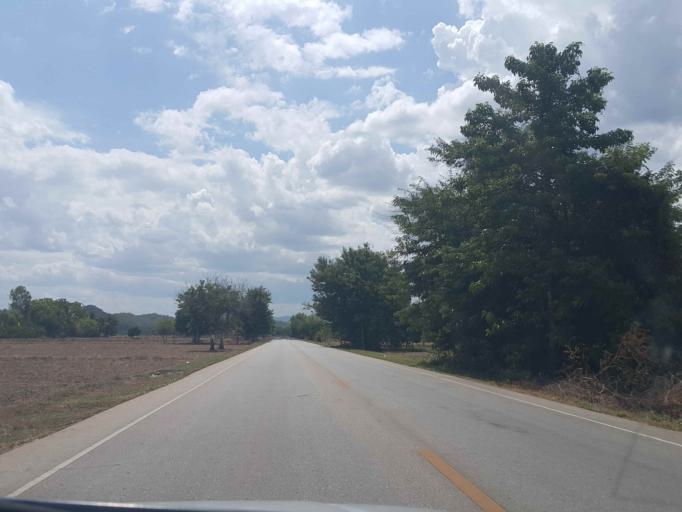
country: TH
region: Sukhothai
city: Thung Saliam
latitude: 17.3368
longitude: 99.6118
